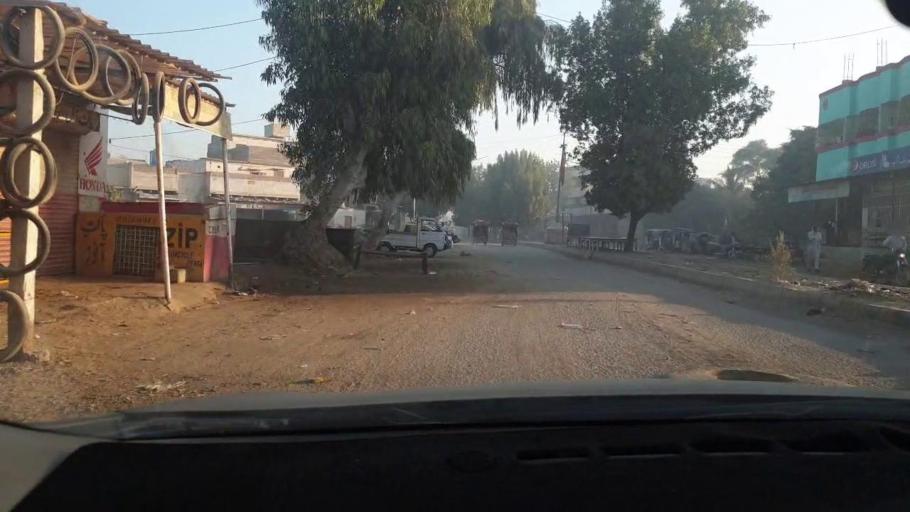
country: PK
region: Sindh
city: Malir Cantonment
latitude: 25.0086
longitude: 67.1576
